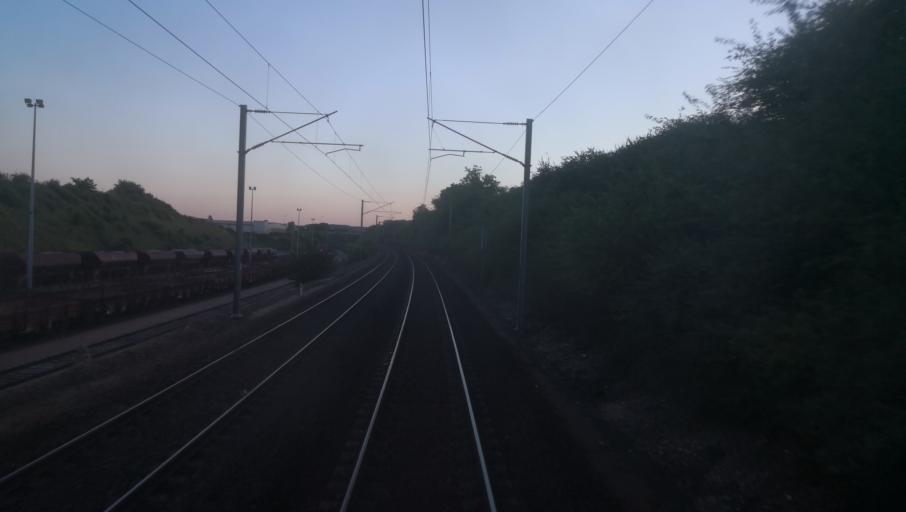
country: FR
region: Ile-de-France
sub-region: Departement des Yvelines
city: Buchelay
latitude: 48.9896
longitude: 1.6869
